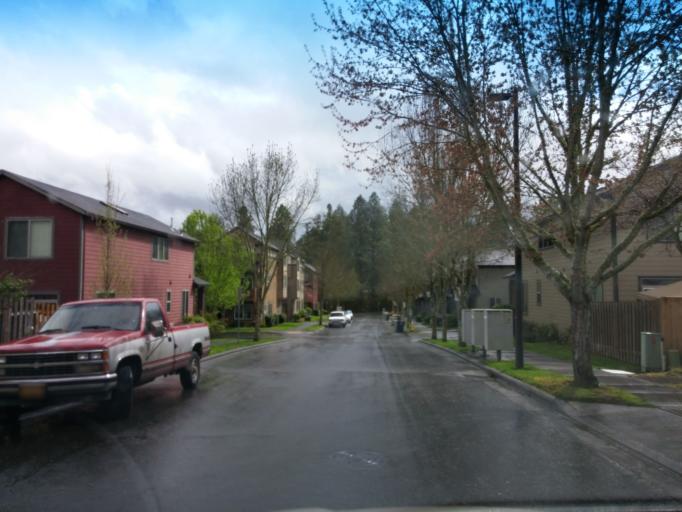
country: US
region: Oregon
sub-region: Washington County
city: Aloha
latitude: 45.5096
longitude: -122.8573
